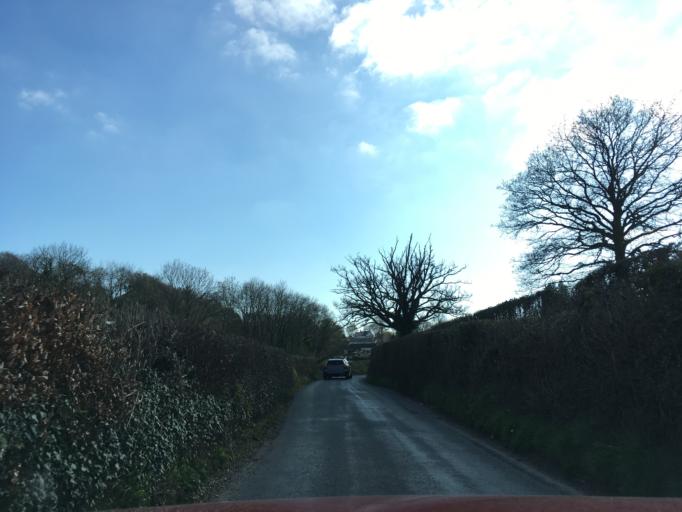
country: GB
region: Wales
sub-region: Torfaen County Borough
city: New Inn
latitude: 51.7126
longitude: -2.9635
